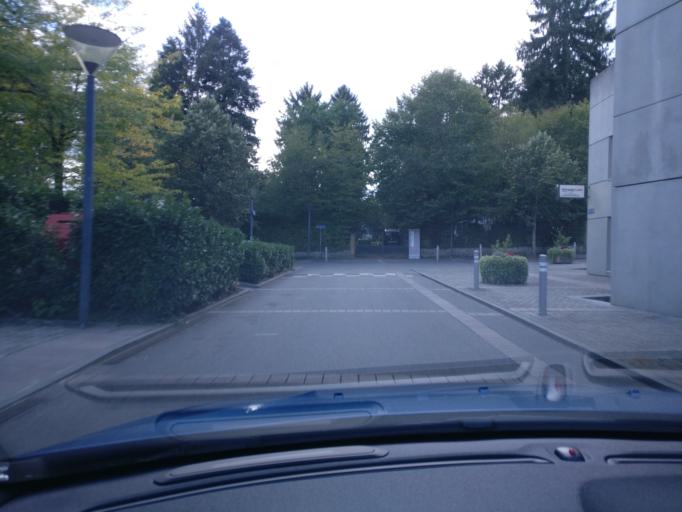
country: CH
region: Geneva
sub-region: Geneva
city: Meyrin
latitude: 46.2280
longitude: 6.0719
